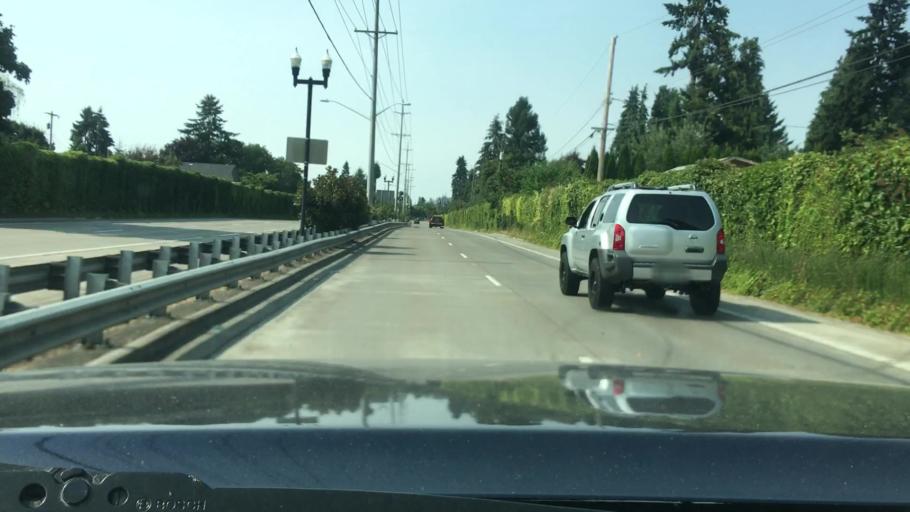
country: US
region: Oregon
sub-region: Lane County
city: Springfield
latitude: 44.0723
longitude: -123.0294
